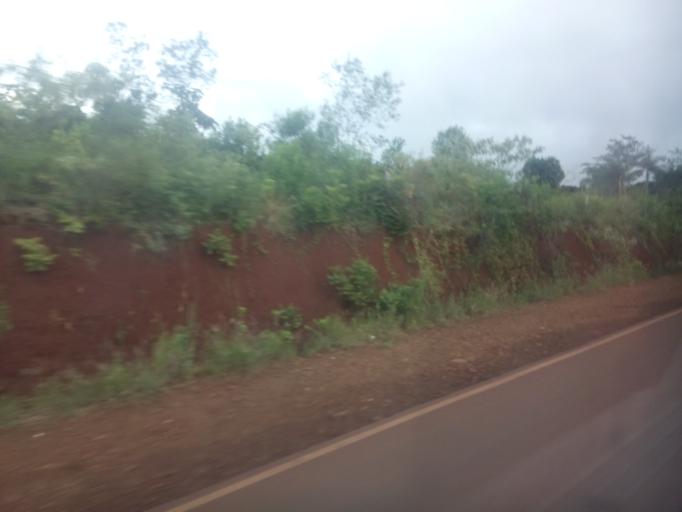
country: AR
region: Misiones
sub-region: Departamento de Obera
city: Obera
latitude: -27.5078
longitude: -55.1385
